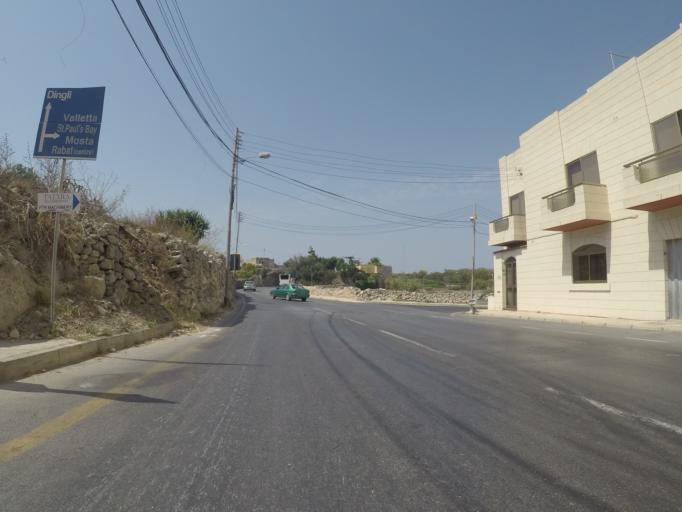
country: MT
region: Ir-Rabat
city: Rabat
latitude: 35.8755
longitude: 14.3964
